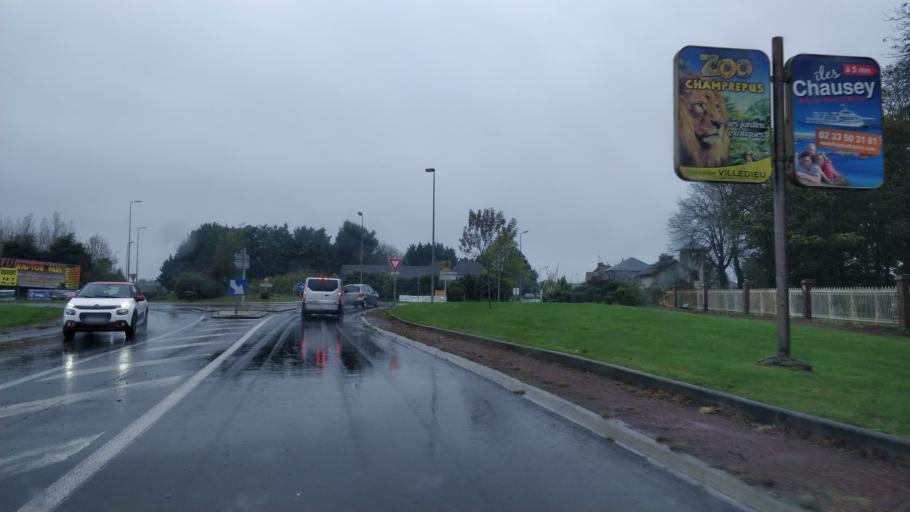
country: FR
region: Lower Normandy
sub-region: Departement de la Manche
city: Brehal
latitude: 48.8667
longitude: -1.5408
